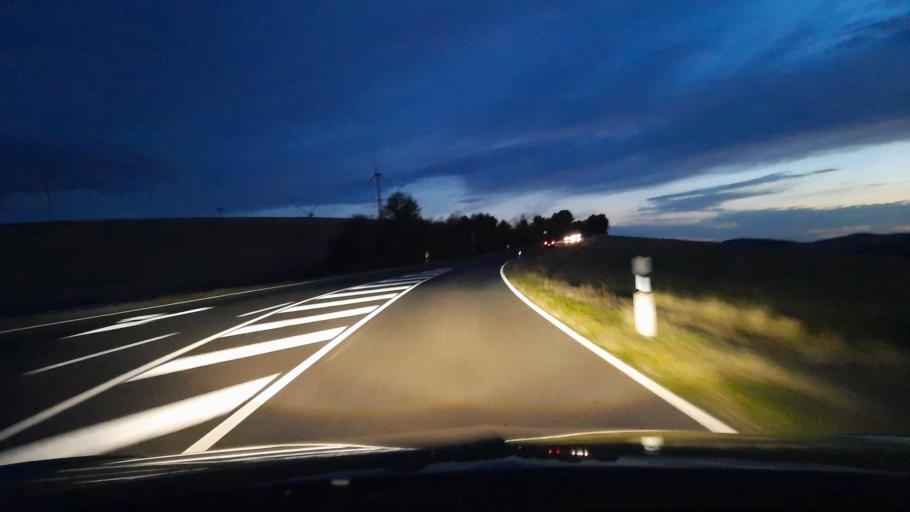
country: DE
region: Rheinland-Pfalz
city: Irsch
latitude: 49.7241
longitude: 6.7110
